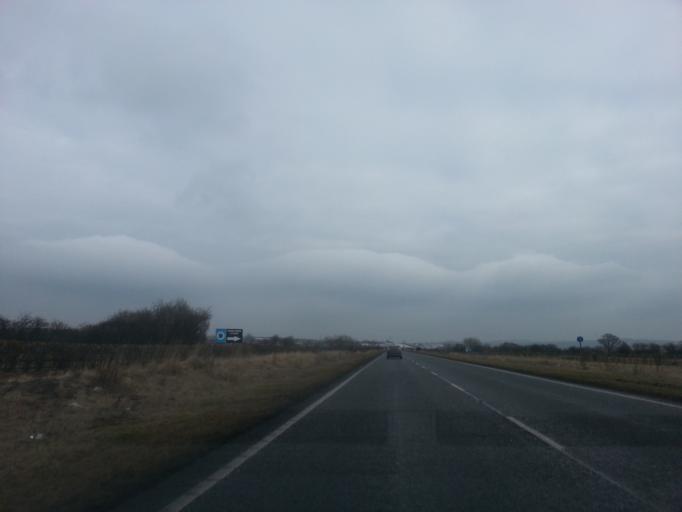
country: GB
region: England
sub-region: County Durham
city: Bishop Auckland
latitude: 54.6285
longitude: -1.7079
